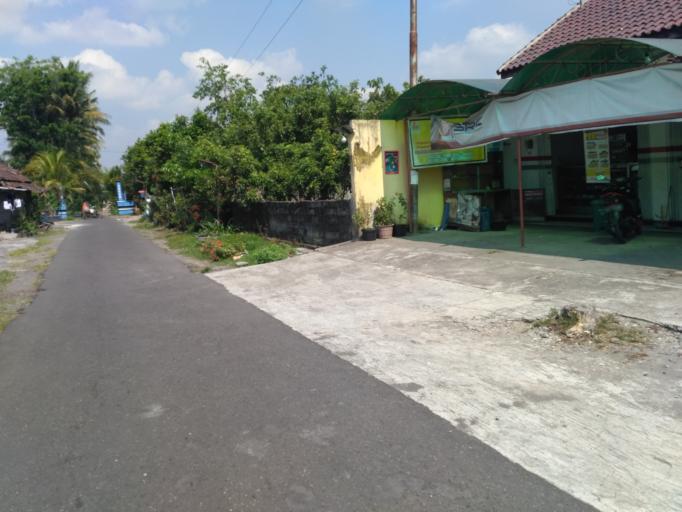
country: ID
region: Daerah Istimewa Yogyakarta
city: Depok
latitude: -7.7136
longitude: 110.4238
